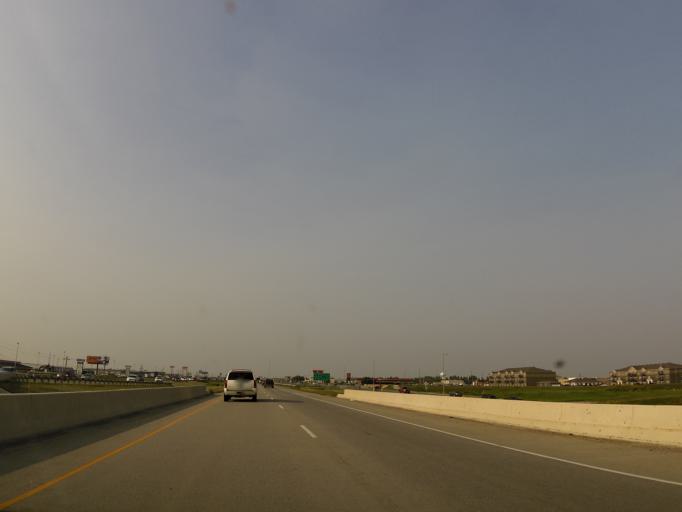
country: US
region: North Dakota
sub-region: Cass County
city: Fargo
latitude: 46.8182
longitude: -96.8393
